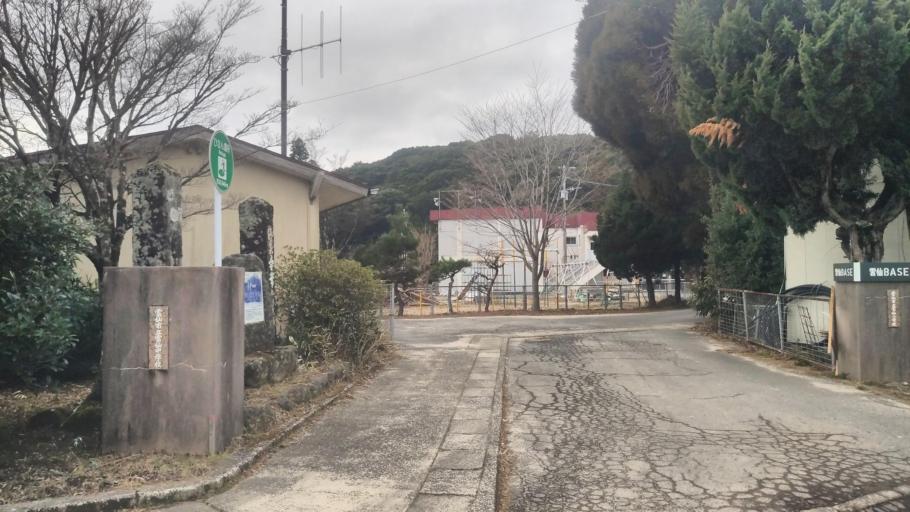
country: JP
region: Nagasaki
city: Shimabara
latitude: 32.7282
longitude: 130.2544
